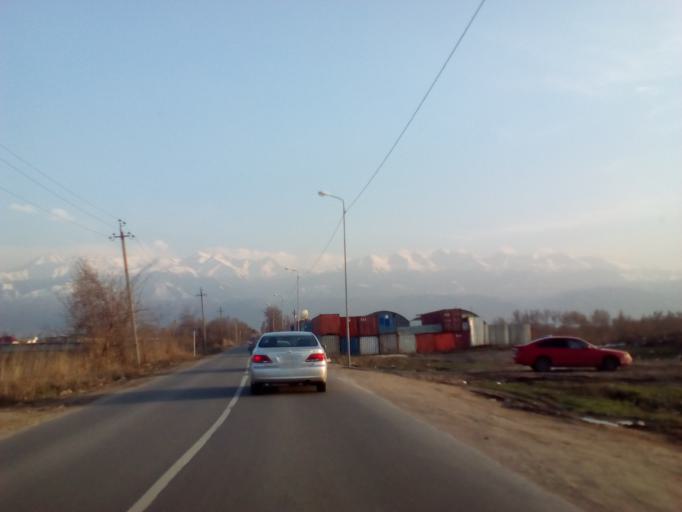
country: KZ
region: Almaty Oblysy
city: Burunday
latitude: 43.2337
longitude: 76.7405
